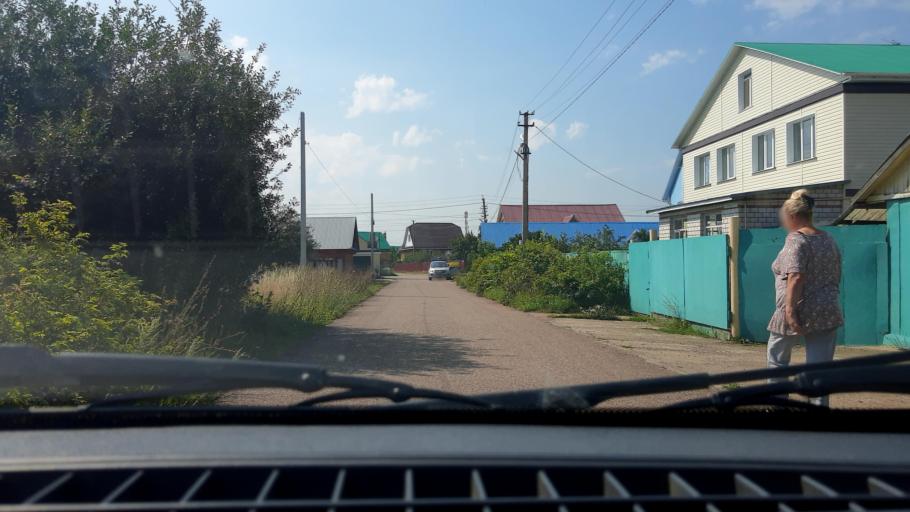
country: RU
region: Bashkortostan
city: Mikhaylovka
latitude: 54.8424
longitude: 55.8295
